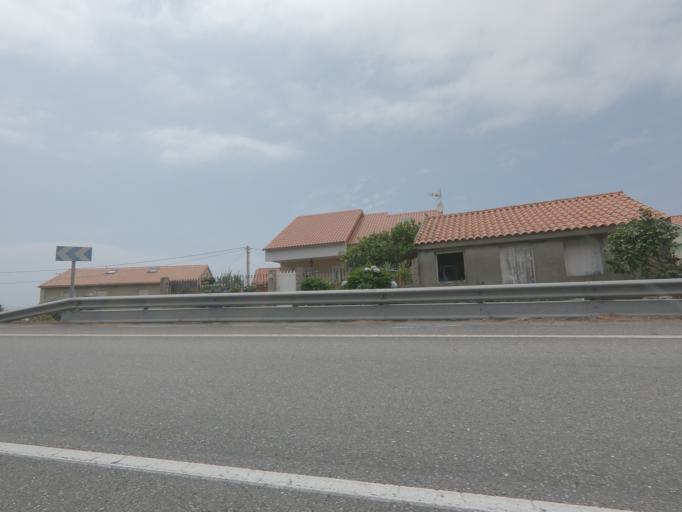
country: ES
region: Galicia
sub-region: Provincia de Pontevedra
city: O Rosal
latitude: 41.9497
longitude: -8.8833
